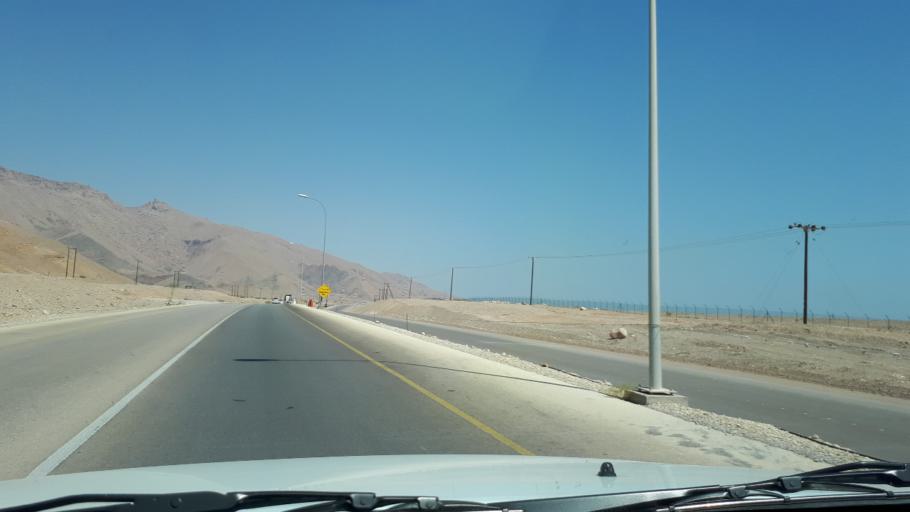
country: OM
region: Ash Sharqiyah
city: Sur
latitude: 22.6253
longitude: 59.4137
